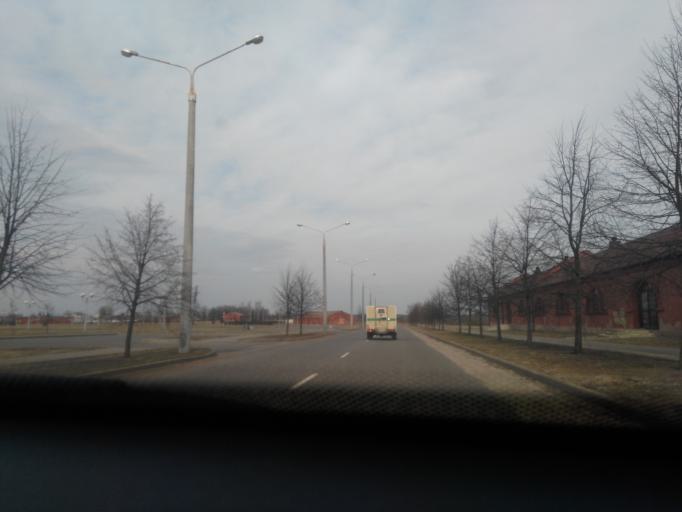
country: BY
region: Mogilev
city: Babruysk
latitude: 53.1406
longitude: 29.2486
